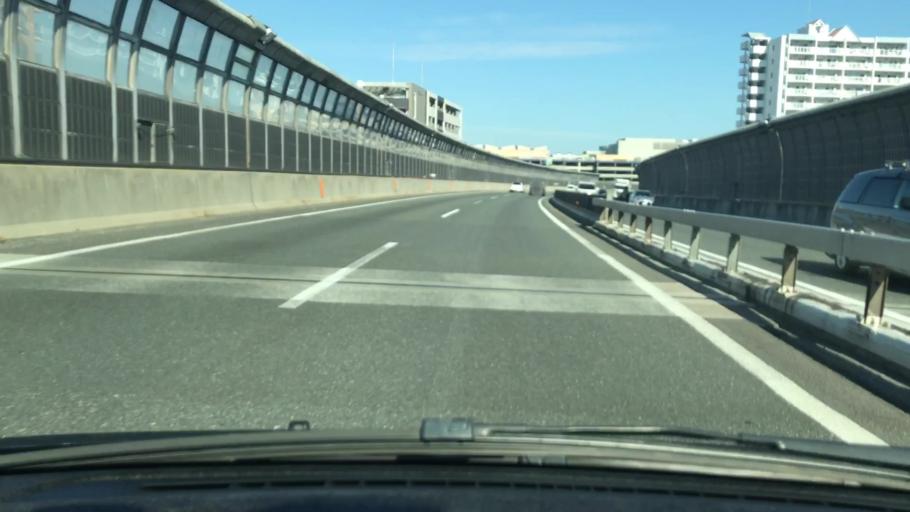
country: JP
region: Hyogo
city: Nishinomiya-hama
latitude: 34.7391
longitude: 135.3595
